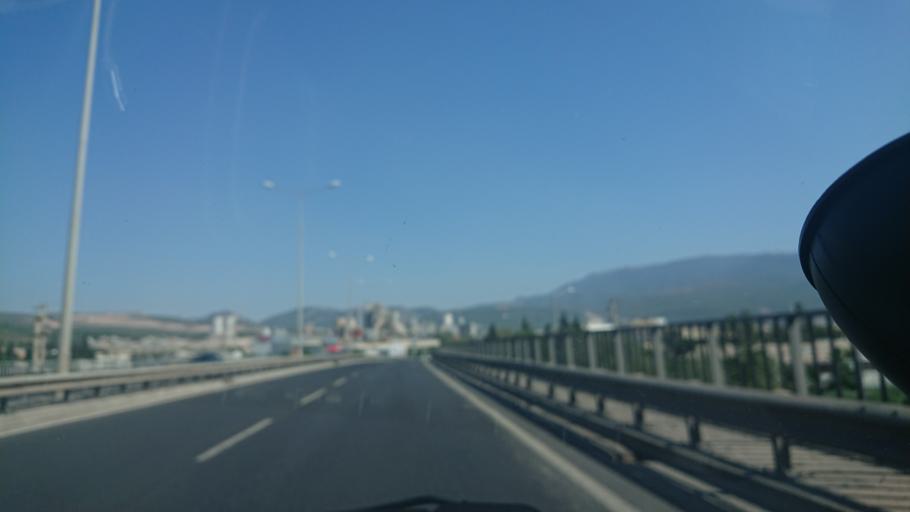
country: TR
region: Izmir
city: Bornova
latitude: 38.4575
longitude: 27.2508
